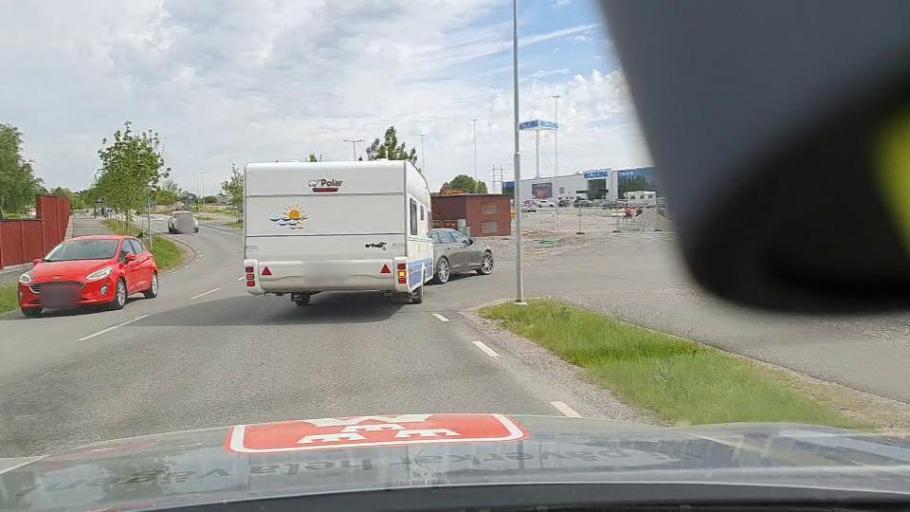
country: SE
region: Soedermanland
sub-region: Eskilstuna Kommun
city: Eskilstuna
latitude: 59.3874
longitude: 16.5304
